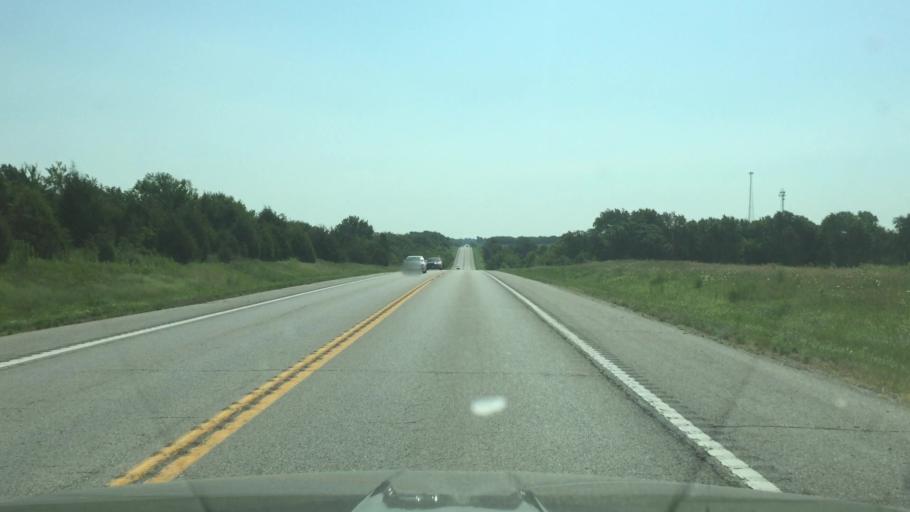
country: US
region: Missouri
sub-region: Pettis County
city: Sedalia
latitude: 38.6942
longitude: -93.1095
